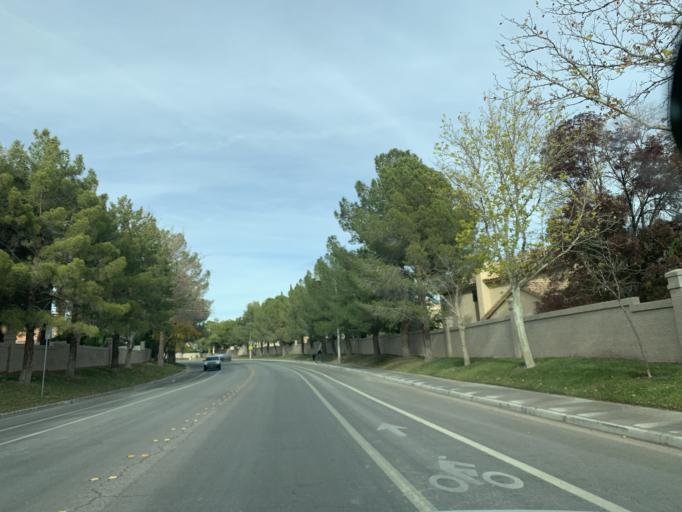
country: US
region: Nevada
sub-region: Clark County
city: Summerlin South
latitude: 36.1355
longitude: -115.3061
